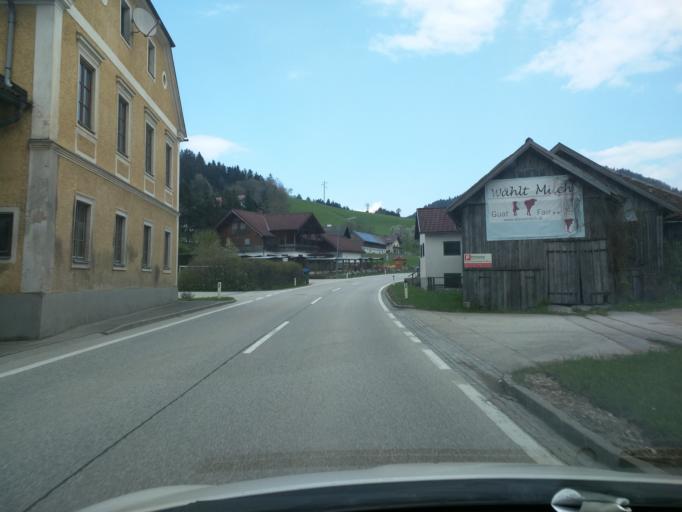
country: AT
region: Lower Austria
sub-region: Politischer Bezirk Amstetten
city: Ybbsitz
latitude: 47.9525
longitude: 14.9191
